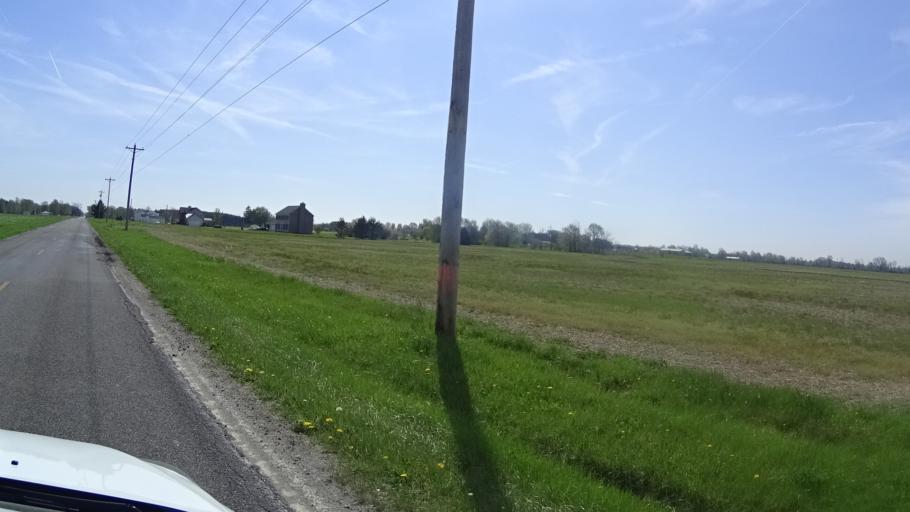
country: US
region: Ohio
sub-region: Lorain County
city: Lagrange
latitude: 41.2747
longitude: -82.1443
